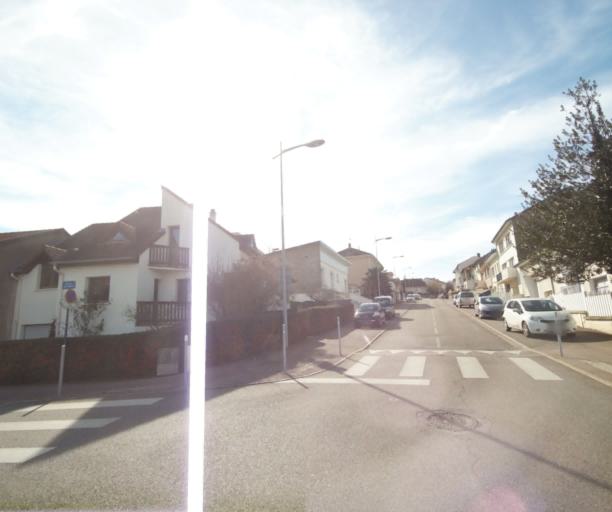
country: FR
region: Lorraine
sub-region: Departement de Meurthe-et-Moselle
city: Villers-les-Nancy
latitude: 48.6640
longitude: 6.1613
